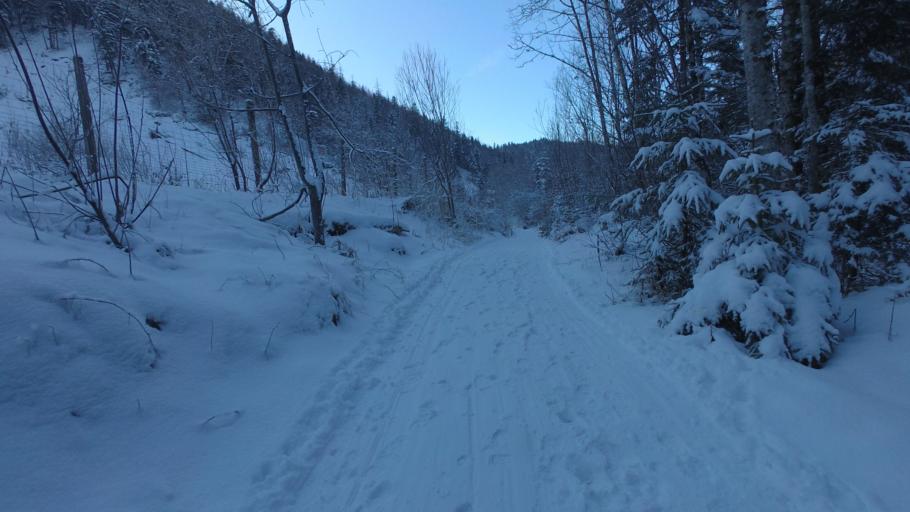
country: DE
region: Bavaria
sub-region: Upper Bavaria
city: Ruhpolding
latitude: 47.7264
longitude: 12.5778
